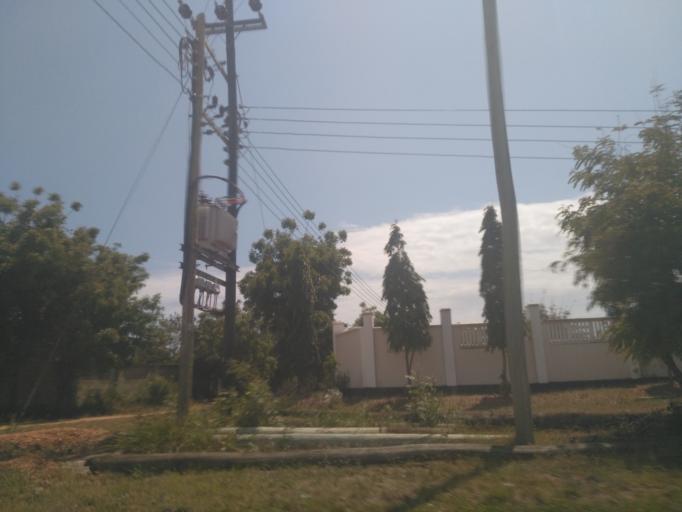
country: TZ
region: Dar es Salaam
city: Magomeni
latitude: -6.7401
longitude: 39.2789
